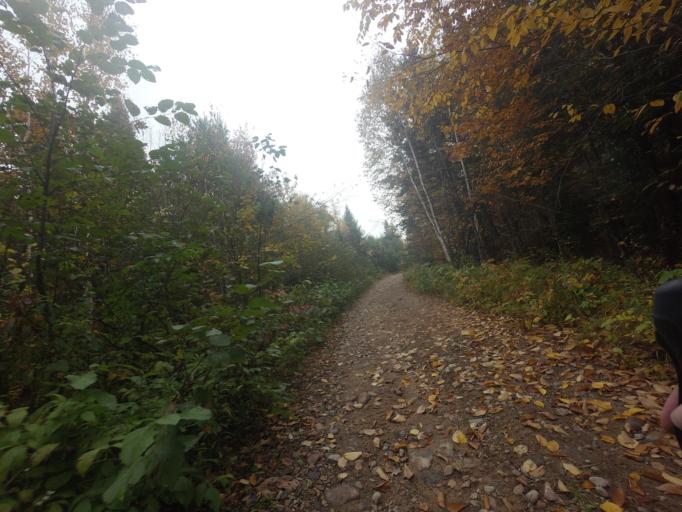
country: CA
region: Ontario
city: Petawawa
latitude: 45.7638
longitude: -77.3694
